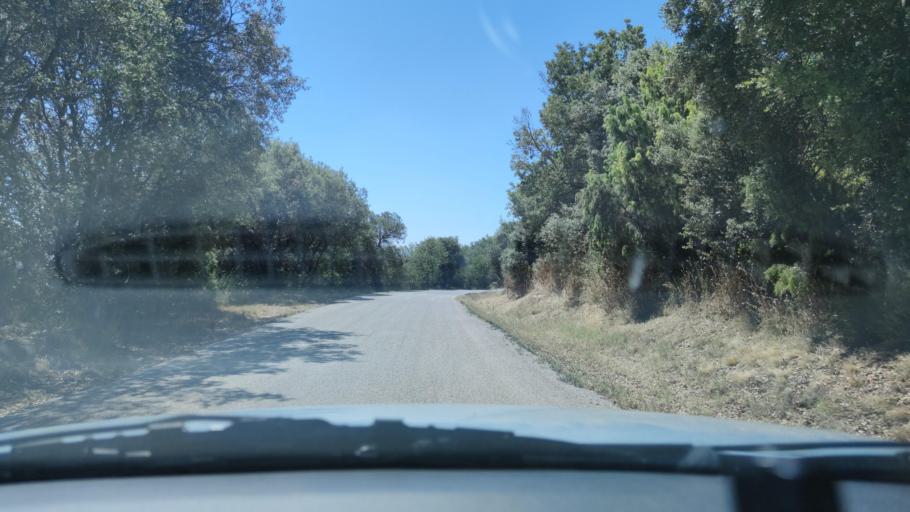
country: ES
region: Catalonia
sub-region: Provincia de Lleida
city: Tora de Riubregos
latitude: 41.8766
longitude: 1.4351
